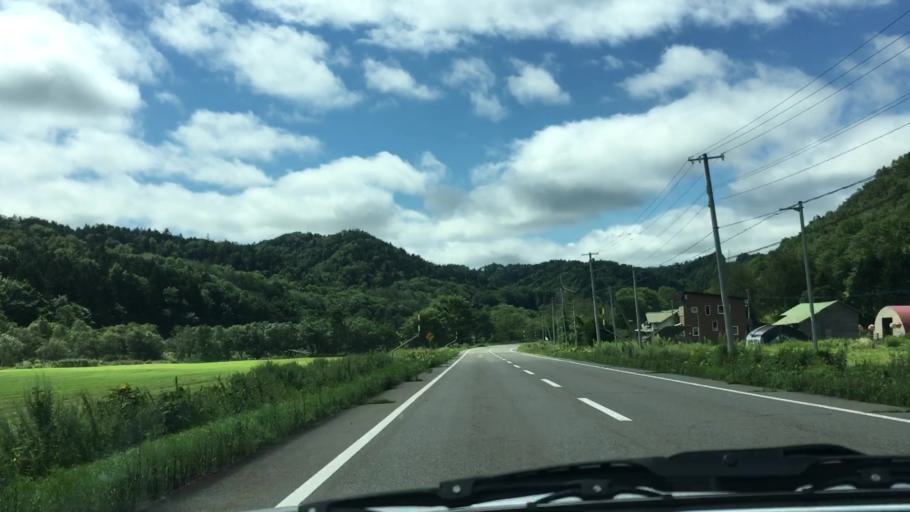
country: JP
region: Hokkaido
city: Kitami
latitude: 43.3635
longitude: 143.8554
